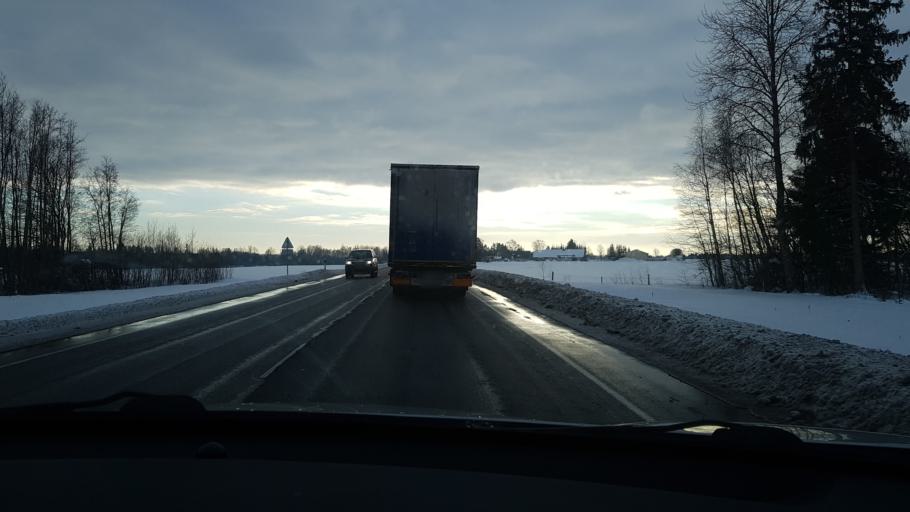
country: EE
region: Jaervamaa
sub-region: Paide linn
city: Paide
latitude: 58.9447
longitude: 25.6440
